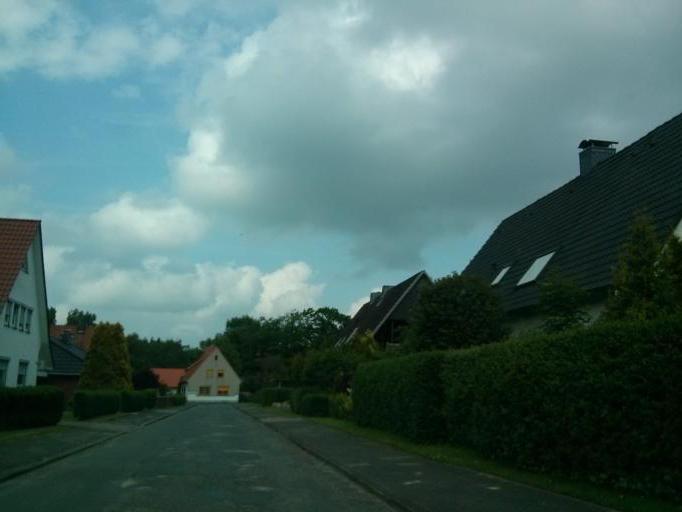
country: DE
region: Lower Saxony
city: Loxstedt
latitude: 53.4963
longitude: 8.6373
